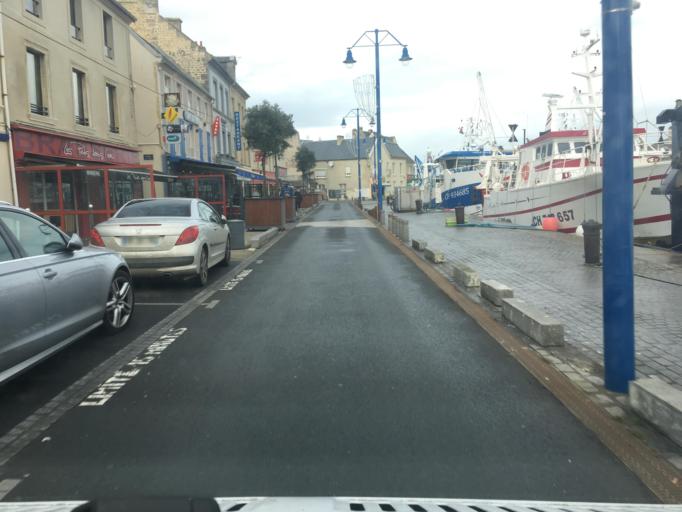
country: FR
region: Lower Normandy
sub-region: Departement du Calvados
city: Port-en-Bessin-Huppain
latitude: 49.3479
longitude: -0.7552
